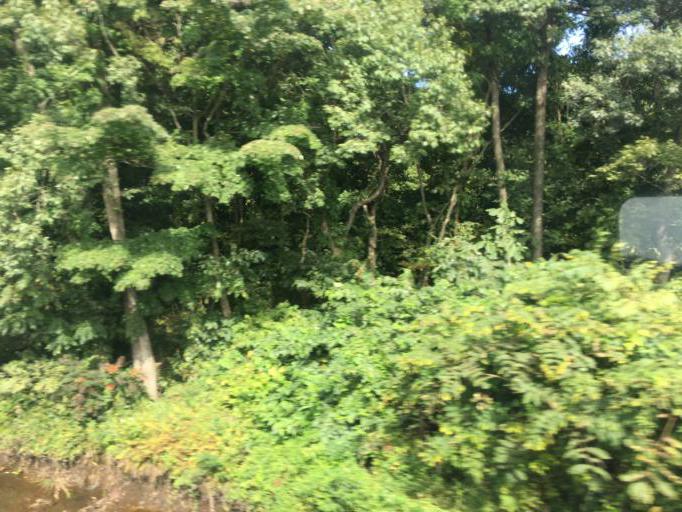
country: JP
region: Iwate
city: Morioka-shi
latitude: 39.8868
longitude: 141.1654
